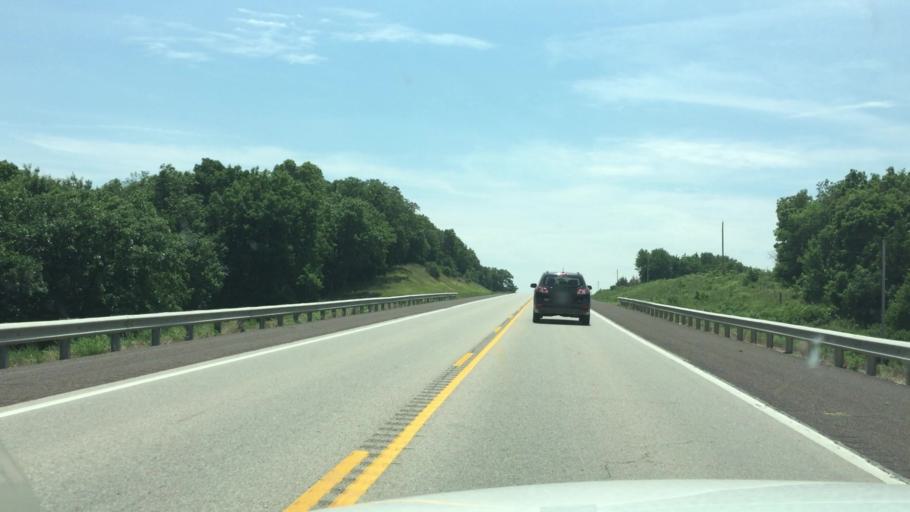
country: US
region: Kansas
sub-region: Jackson County
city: Holton
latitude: 39.5444
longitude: -95.7483
